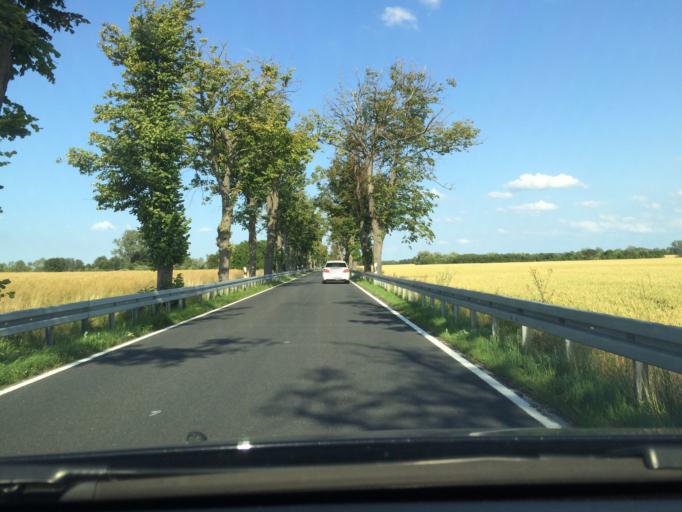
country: DE
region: Mecklenburg-Vorpommern
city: Velgast
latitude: 54.3312
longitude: 12.8481
